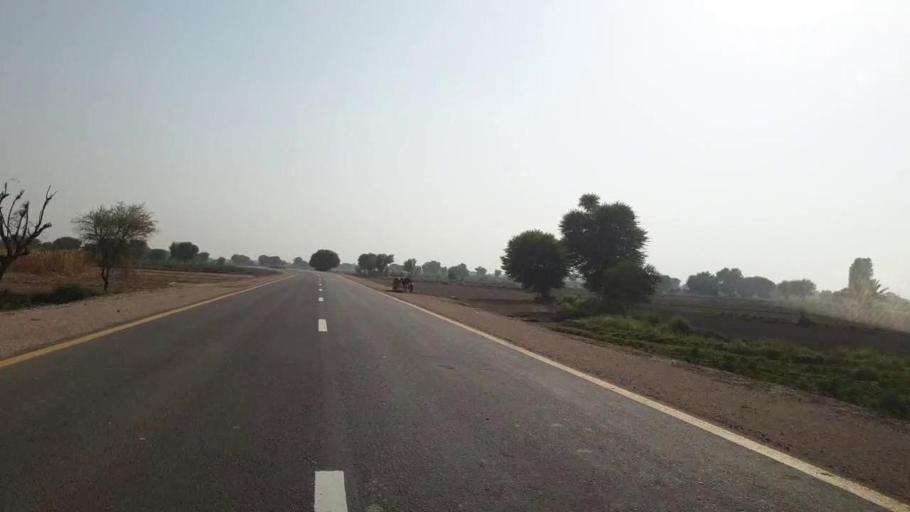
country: PK
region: Sindh
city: Bhan
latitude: 26.5100
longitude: 67.7846
